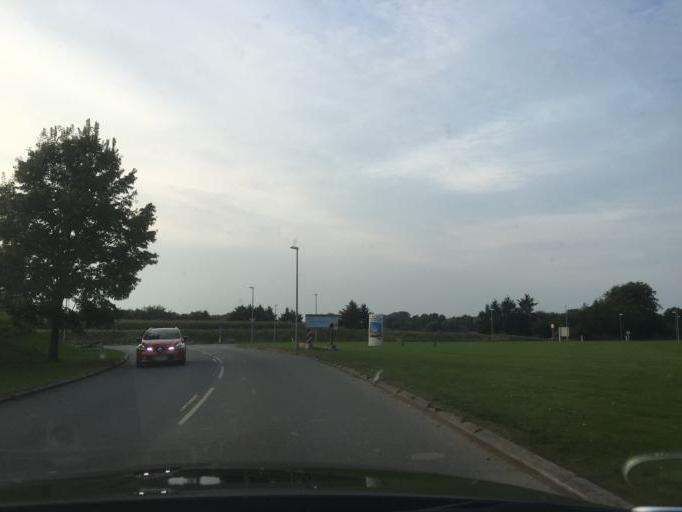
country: DK
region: South Denmark
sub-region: Esbjerg Kommune
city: Bramming
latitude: 55.4814
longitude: 8.6939
